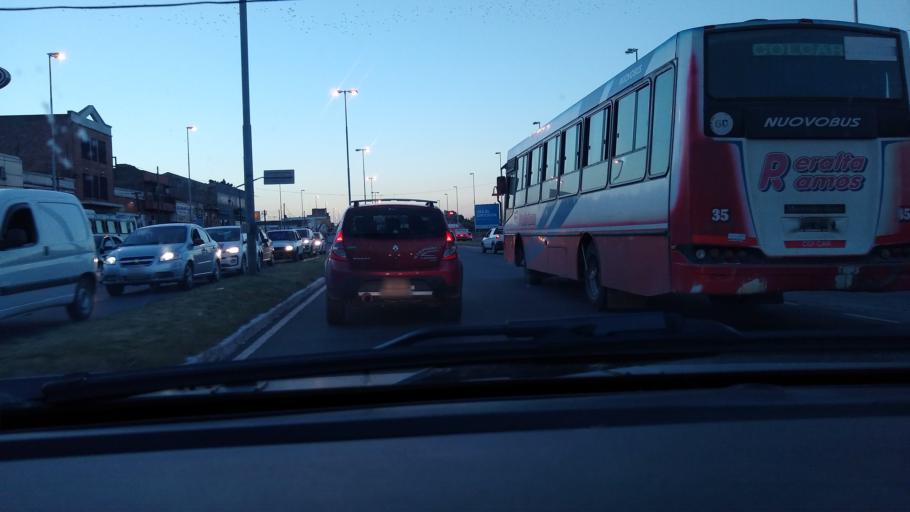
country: AR
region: Buenos Aires
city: San Justo
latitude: -34.6887
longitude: -58.5562
